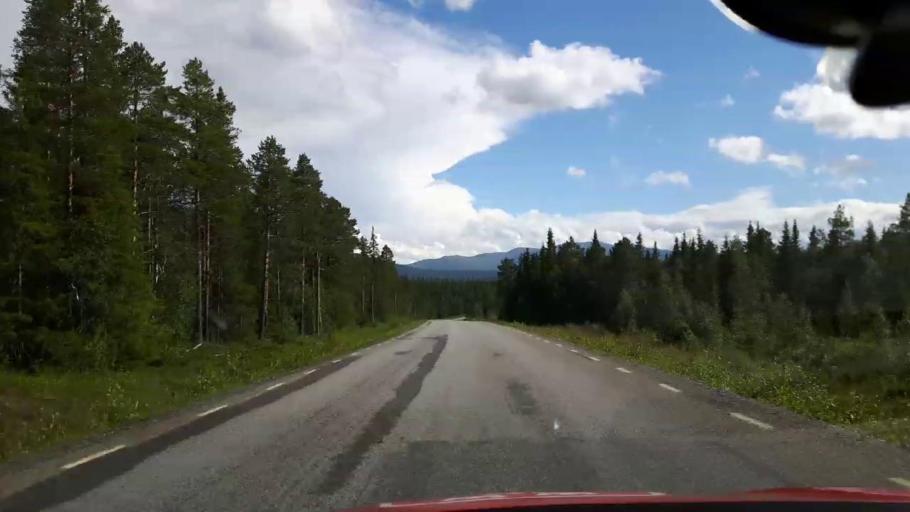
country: SE
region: Jaemtland
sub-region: Are Kommun
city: Are
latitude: 63.2249
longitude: 13.1613
